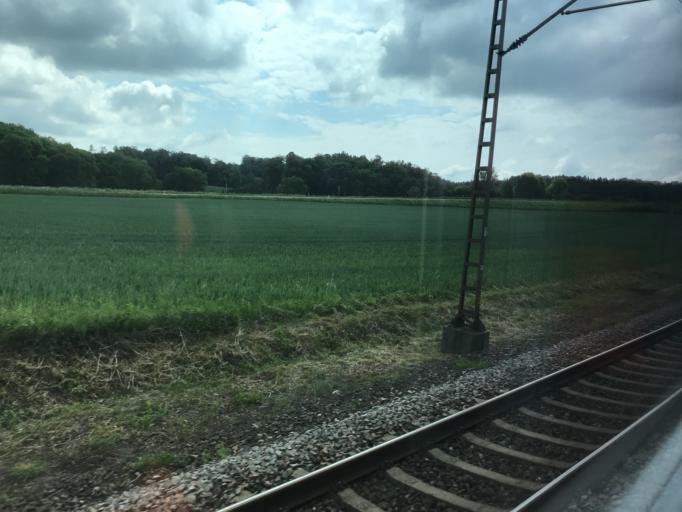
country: DE
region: Baden-Wuerttemberg
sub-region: Tuebingen Region
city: Westerstetten
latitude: 48.5067
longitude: 9.9501
